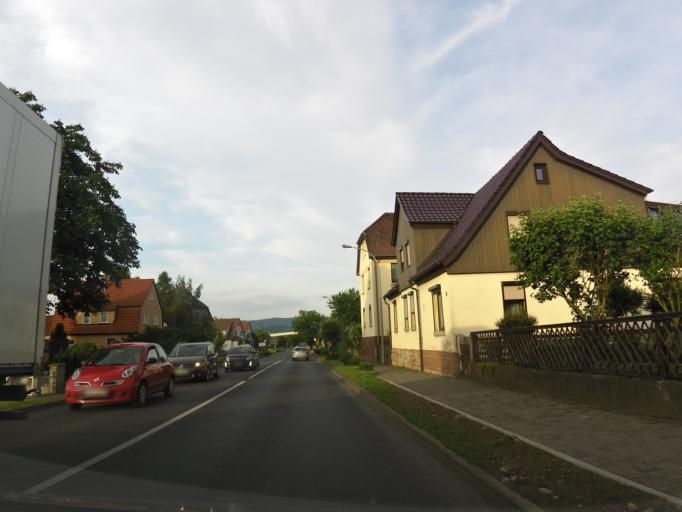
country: DE
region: Thuringia
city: Immelborn
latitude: 50.7946
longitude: 10.2801
